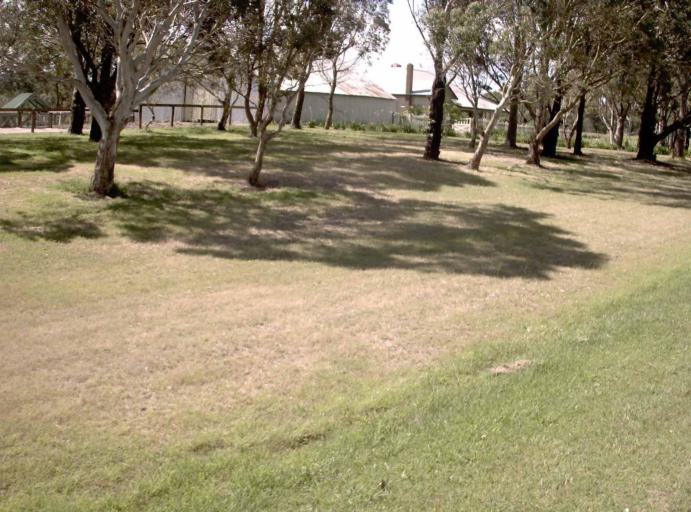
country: AU
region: Victoria
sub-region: Latrobe
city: Traralgon
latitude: -38.1517
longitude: 146.5221
